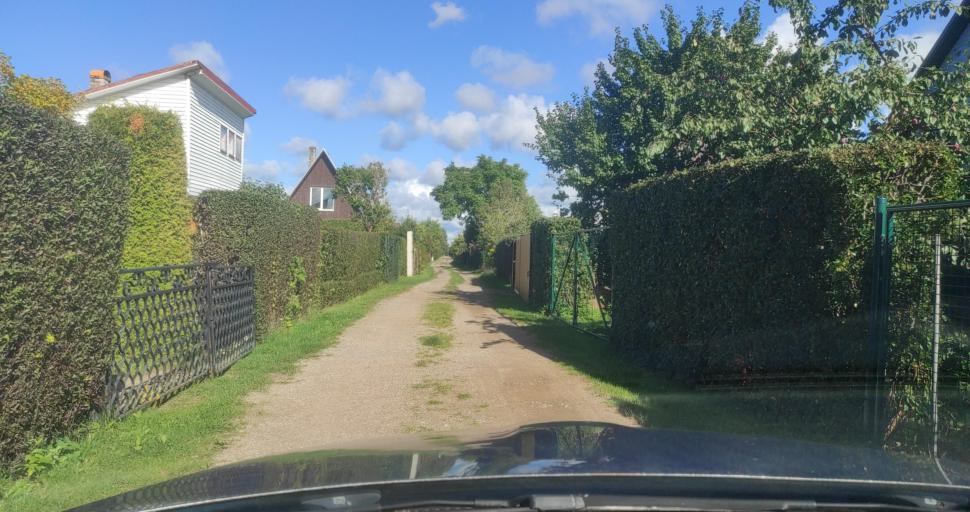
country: LV
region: Ventspils
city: Ventspils
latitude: 57.3686
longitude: 21.6008
